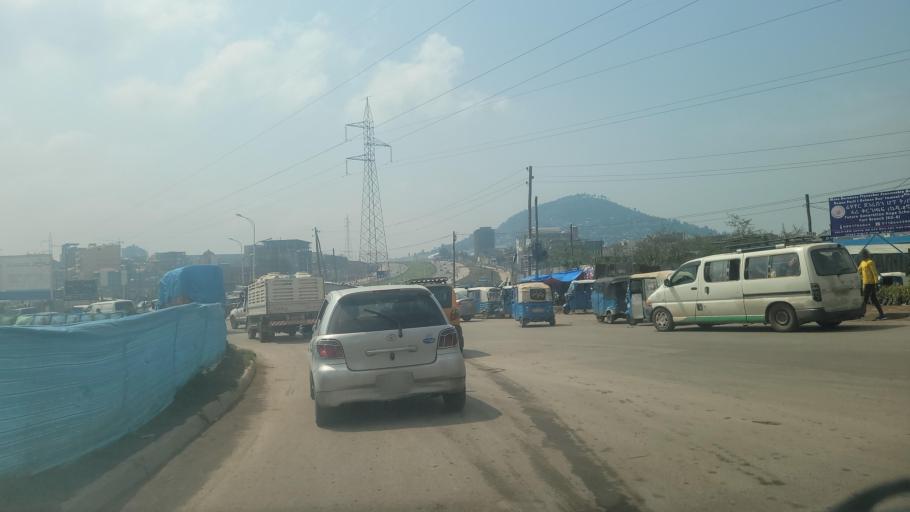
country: ET
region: Adis Abeba
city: Addis Ababa
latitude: 8.9540
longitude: 38.6966
